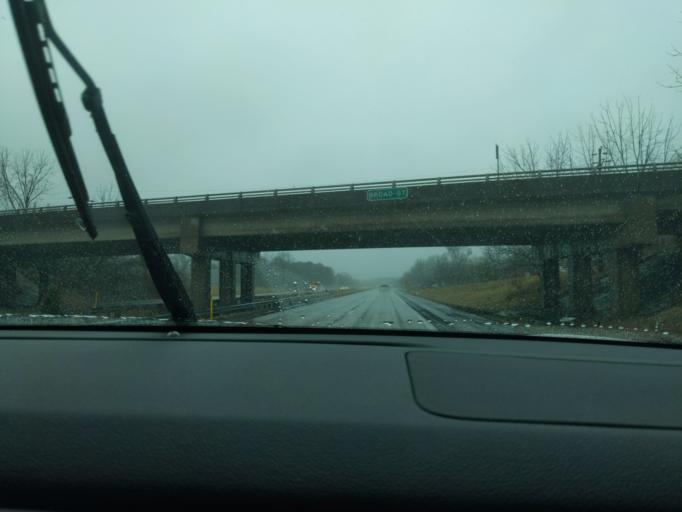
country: US
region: Pennsylvania
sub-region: Bucks County
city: Doylestown
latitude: 40.3216
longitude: -75.1425
